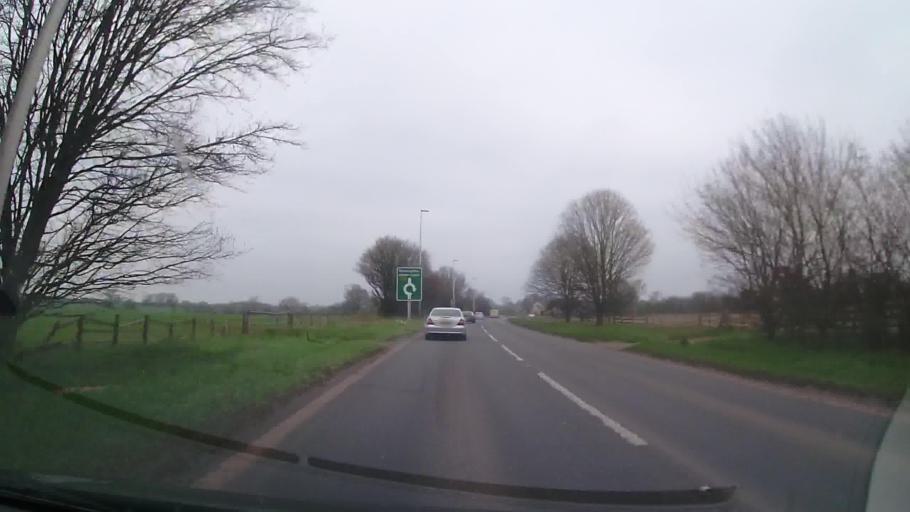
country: GB
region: England
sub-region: Shropshire
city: Market Drayton
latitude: 52.9084
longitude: -2.5036
